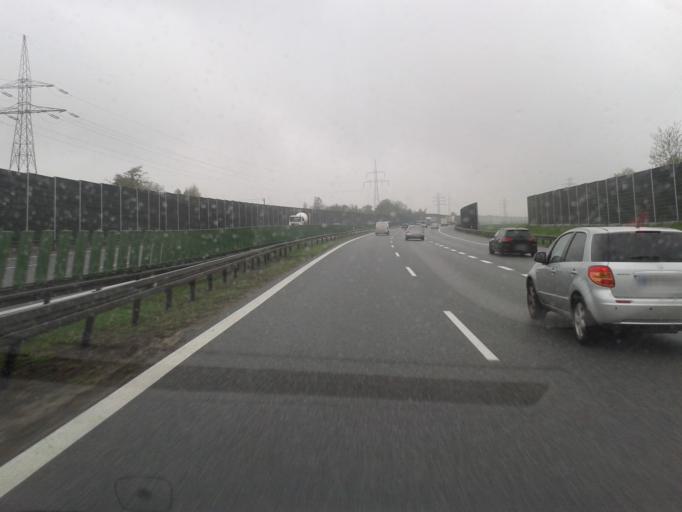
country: PL
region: Lesser Poland Voivodeship
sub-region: Powiat wielicki
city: Czarnochowice
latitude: 50.0075
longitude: 20.0532
